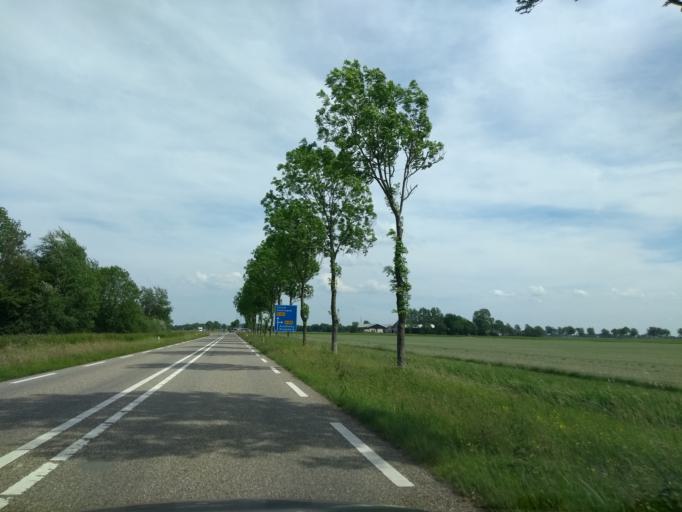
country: NL
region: Groningen
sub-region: Gemeente De Marne
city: Ulrum
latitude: 53.3650
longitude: 6.3018
